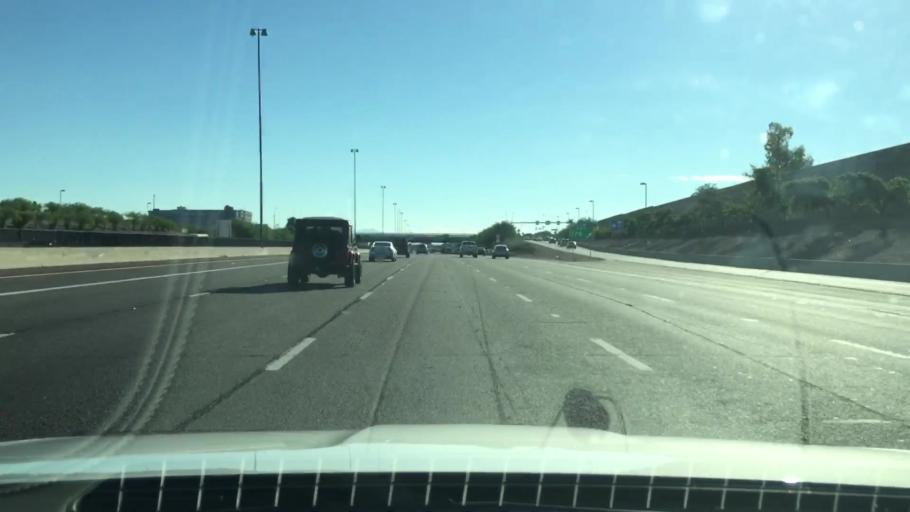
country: US
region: Arizona
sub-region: Maricopa County
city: San Carlos
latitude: 33.3855
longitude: -111.8621
